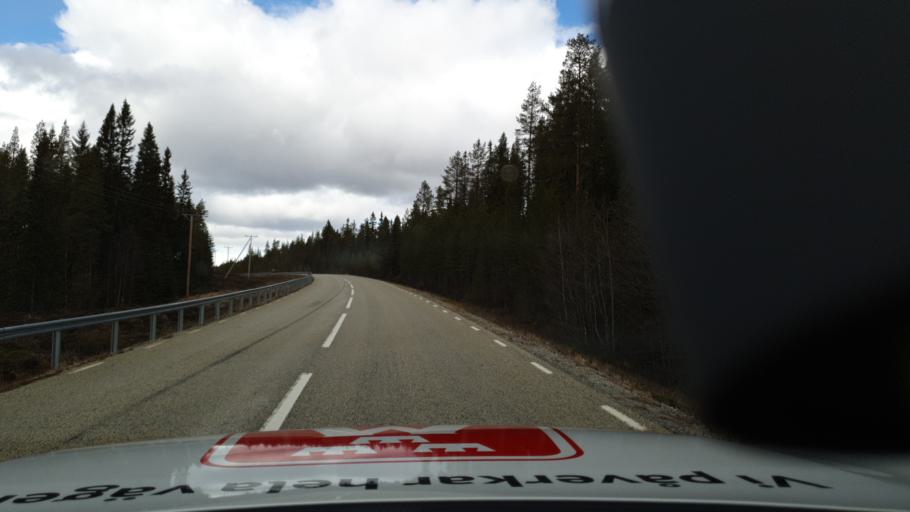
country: SE
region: Jaemtland
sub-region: Are Kommun
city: Jarpen
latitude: 62.7865
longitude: 13.6931
